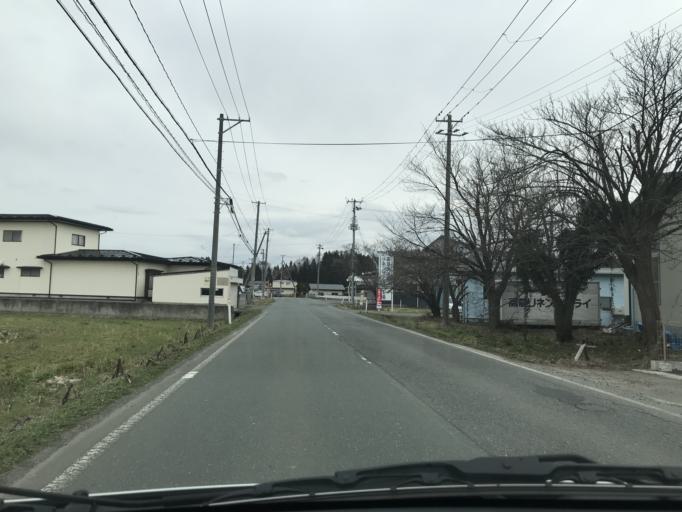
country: JP
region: Iwate
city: Kitakami
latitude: 39.2694
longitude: 141.1116
